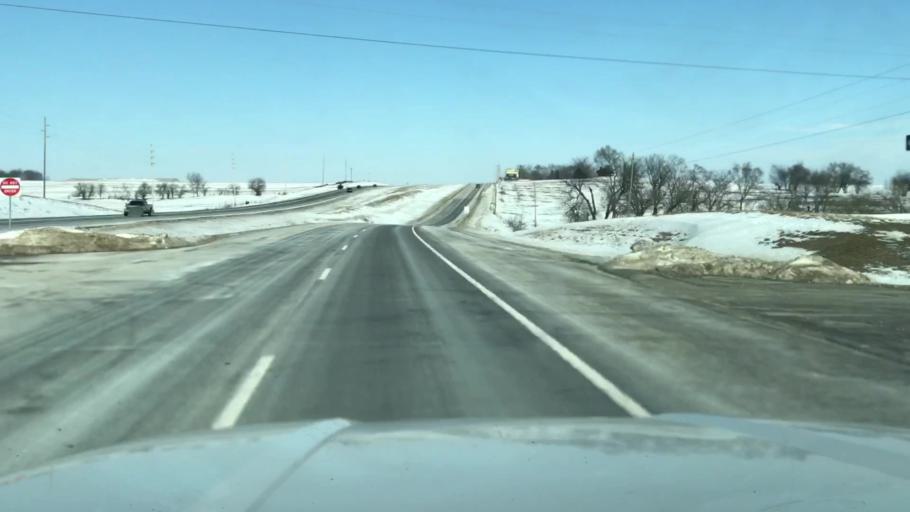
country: US
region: Missouri
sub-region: Andrew County
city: Savannah
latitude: 40.1063
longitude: -94.8697
